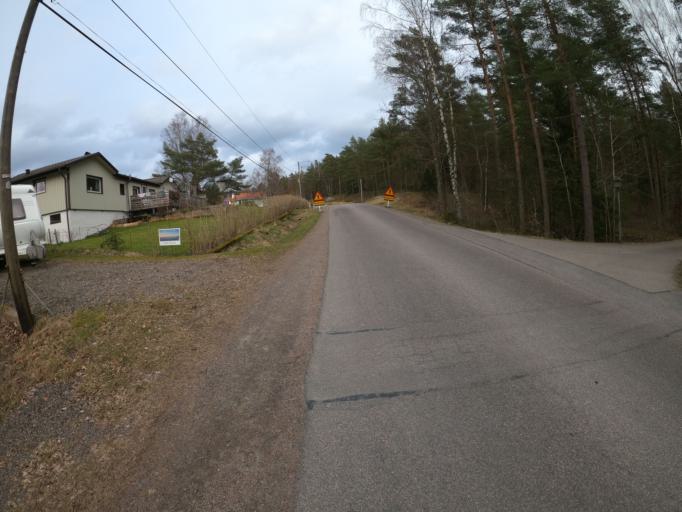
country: SE
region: Vaestra Goetaland
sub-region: Harryda Kommun
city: Molnlycke
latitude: 57.6170
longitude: 12.1016
